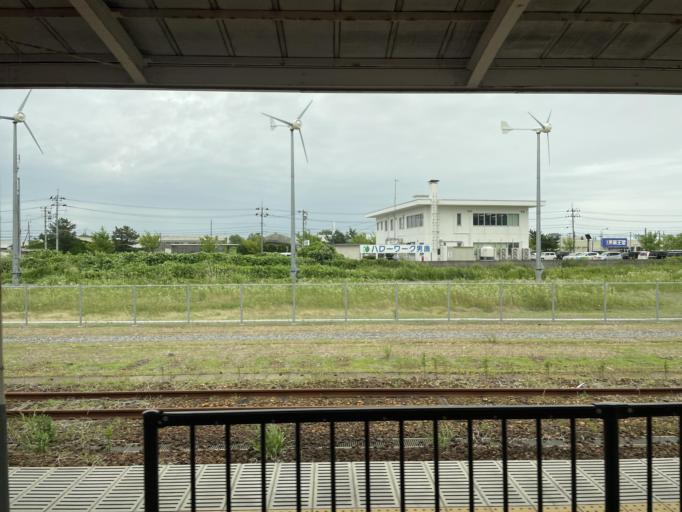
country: JP
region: Akita
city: Tenno
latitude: 39.8848
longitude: 139.8487
